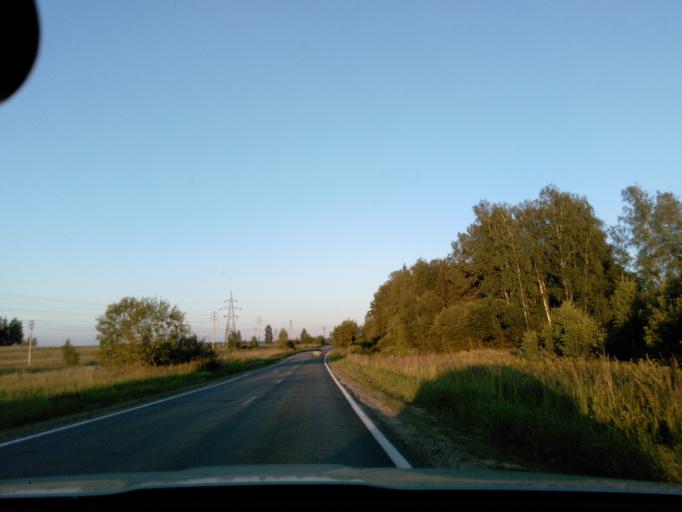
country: RU
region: Moskovskaya
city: Solnechnogorsk
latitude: 56.1216
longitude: 36.8980
